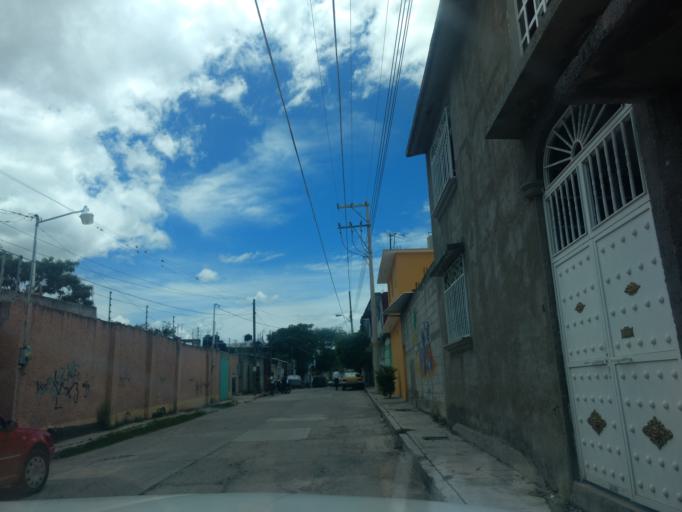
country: MX
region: Oaxaca
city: Ciudad de Huajuapam de Leon
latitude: 17.8056
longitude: -97.7833
